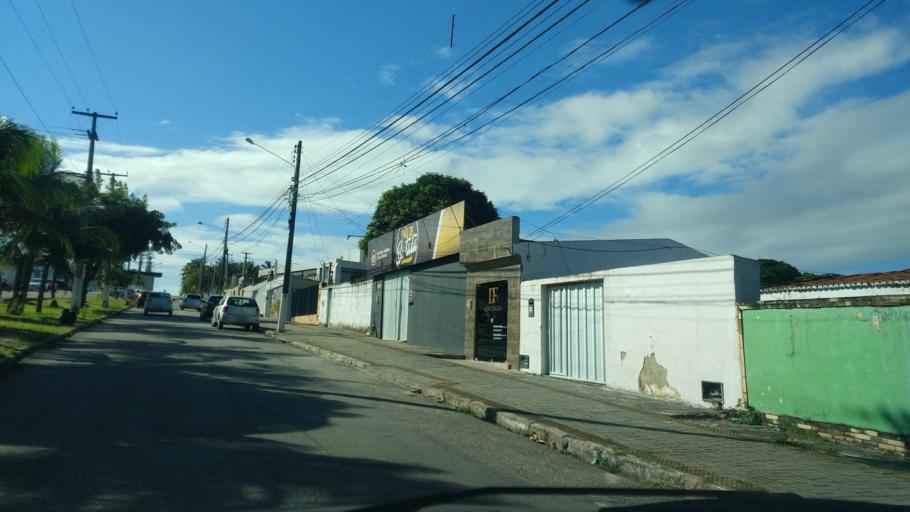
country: BR
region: Rio Grande do Norte
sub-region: Natal
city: Natal
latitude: -5.8311
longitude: -35.2069
